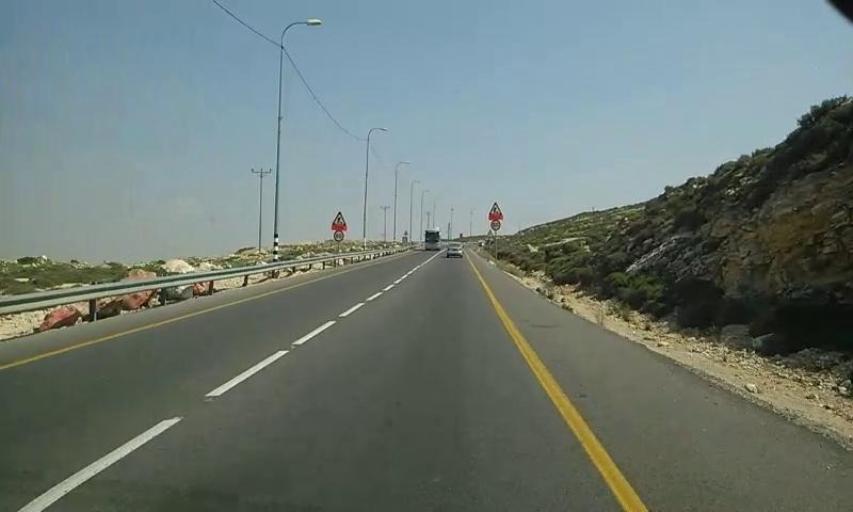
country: PS
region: West Bank
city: Jaba`
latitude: 31.8608
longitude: 35.2632
